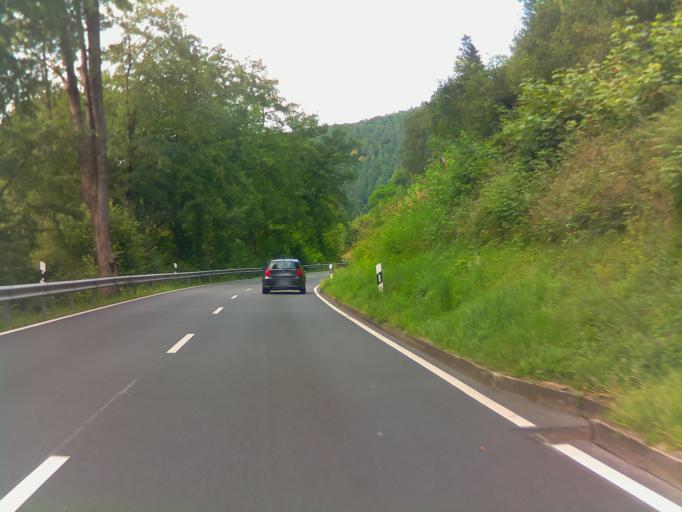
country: DE
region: Baden-Wuerttemberg
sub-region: Karlsruhe Region
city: Schonau
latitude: 49.4236
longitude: 8.8086
